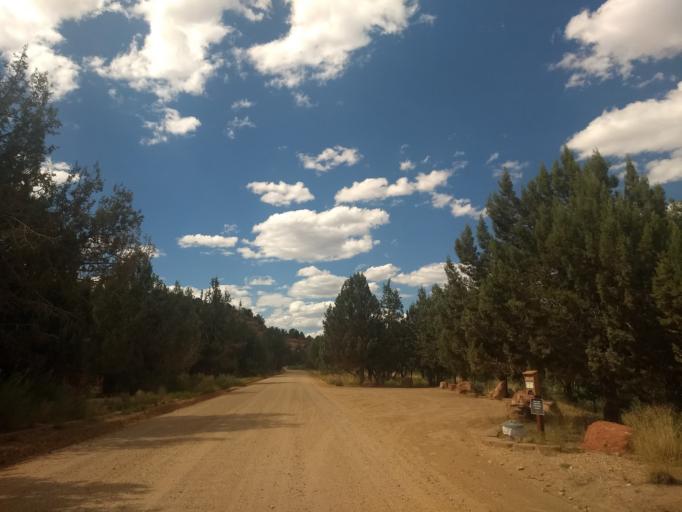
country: US
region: Utah
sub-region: Kane County
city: Kanab
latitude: 37.1479
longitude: -112.5398
